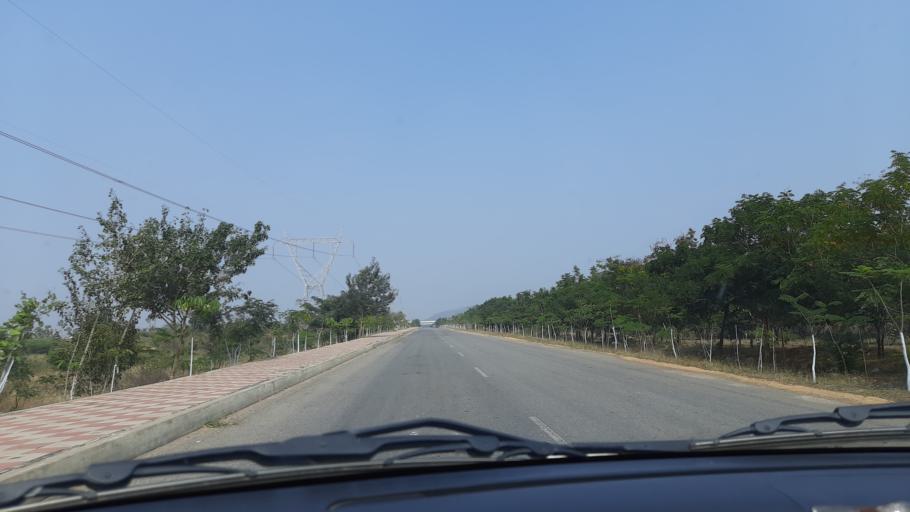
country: IN
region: Telangana
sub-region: Rangareddi
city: Lal Bahadur Nagar
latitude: 17.3018
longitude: 78.6538
